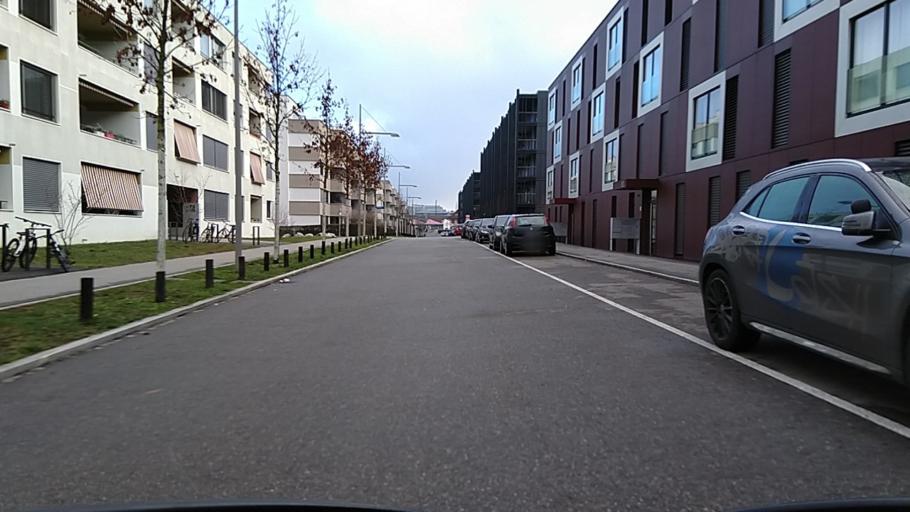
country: CH
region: Bern
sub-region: Bern-Mittelland District
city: Wohlen
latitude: 46.9450
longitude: 7.3781
